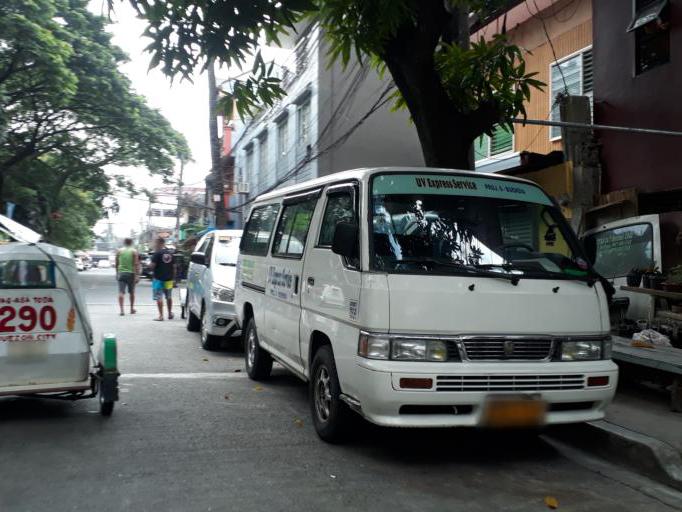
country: PH
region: Calabarzon
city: Bagong Pagasa
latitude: 14.6624
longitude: 121.0329
